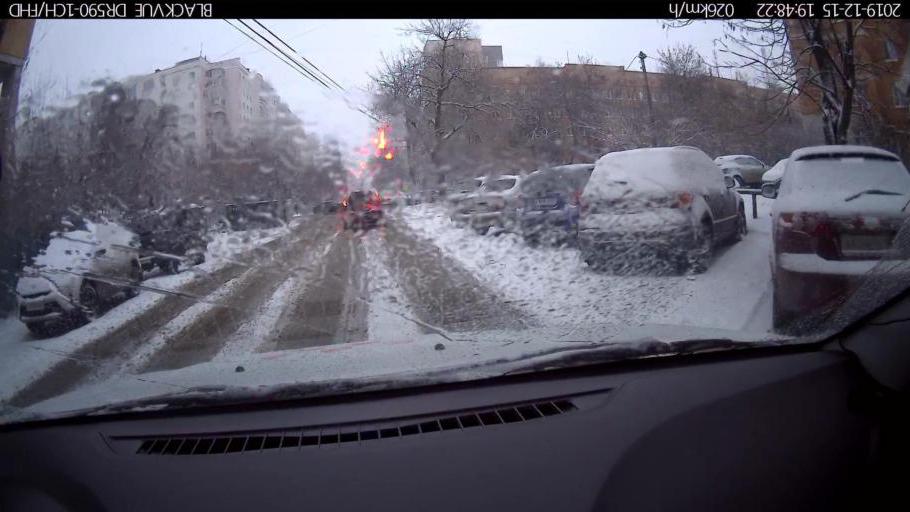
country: RU
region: Nizjnij Novgorod
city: Nizhniy Novgorod
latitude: 56.3150
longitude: 44.0248
